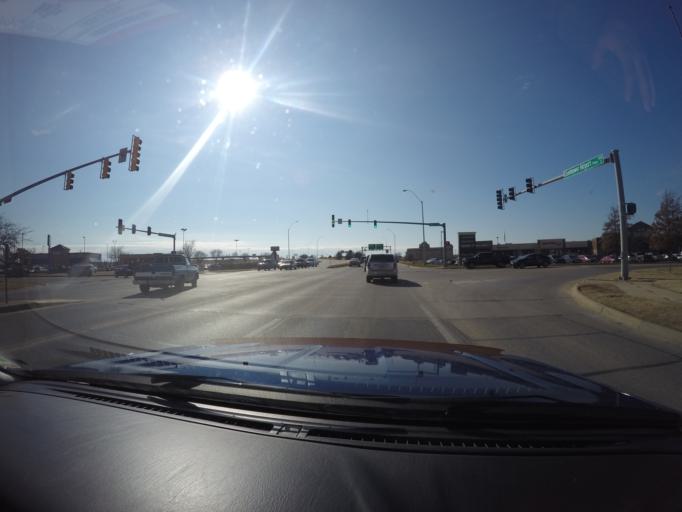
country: US
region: Kansas
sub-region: Sedgwick County
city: Wichita
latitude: 37.6769
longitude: -97.4269
